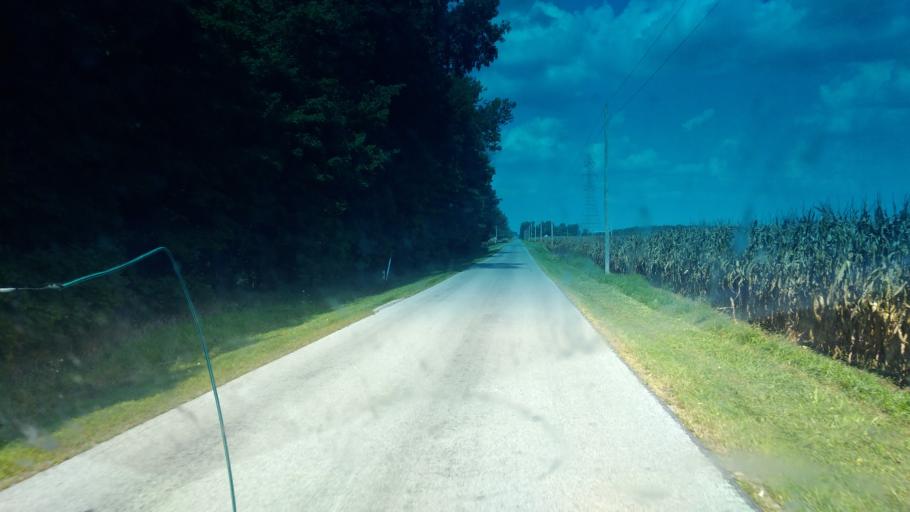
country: US
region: Ohio
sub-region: Hardin County
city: Ada
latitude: 40.6874
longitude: -83.8800
